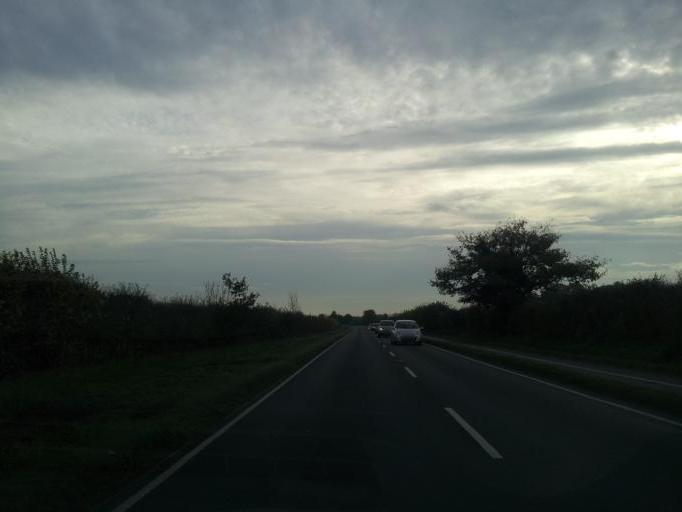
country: GB
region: England
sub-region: Cambridgeshire
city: Duxford
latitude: 52.0973
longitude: 0.1799
